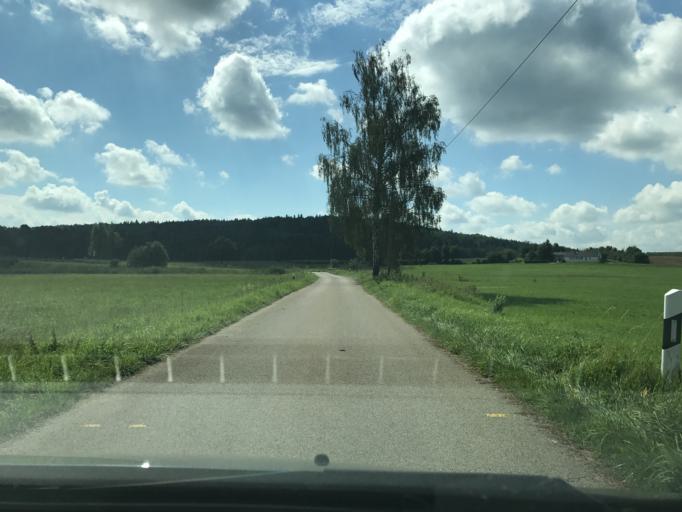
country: DE
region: Bavaria
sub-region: Regierungsbezirk Mittelfranken
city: Rockingen
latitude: 49.0365
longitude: 10.5483
